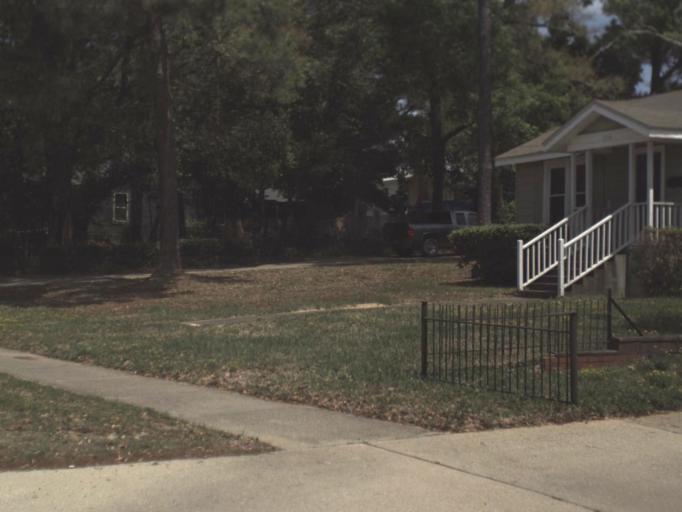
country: US
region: Florida
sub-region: Escambia County
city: East Pensacola Heights
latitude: 30.4345
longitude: -87.1823
